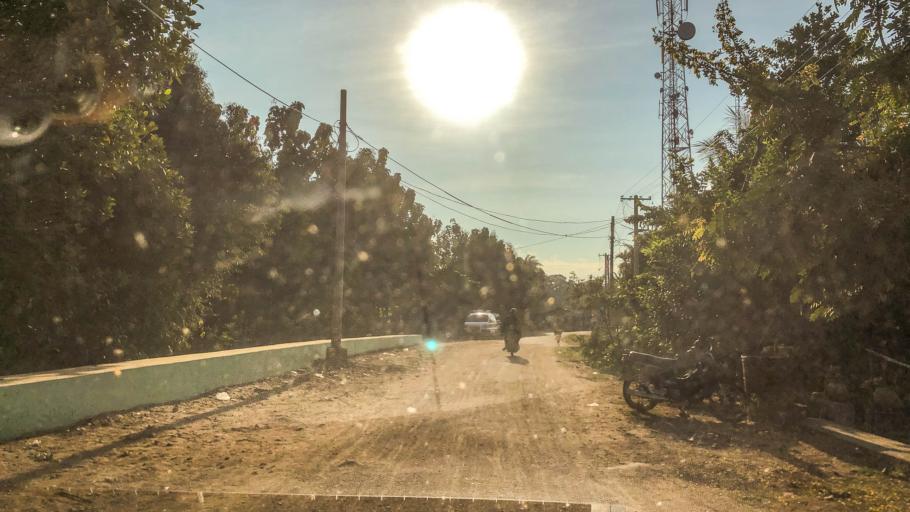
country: MM
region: Magway
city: Magway
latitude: 19.9711
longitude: 95.0424
